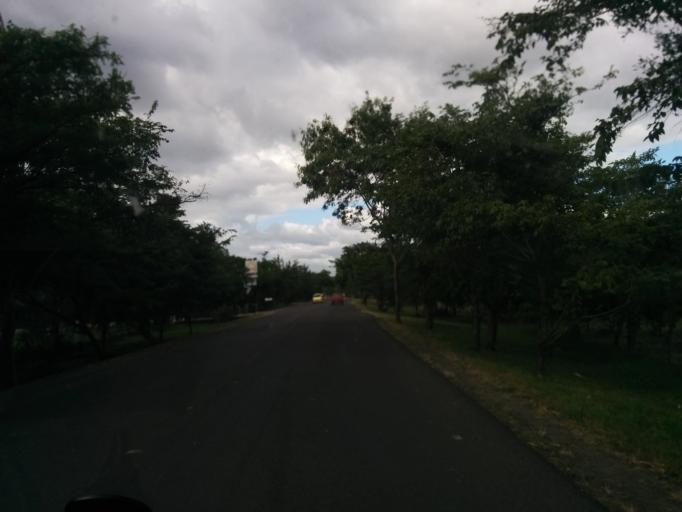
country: NI
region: Esteli
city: Esteli
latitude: 13.1444
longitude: -86.3678
